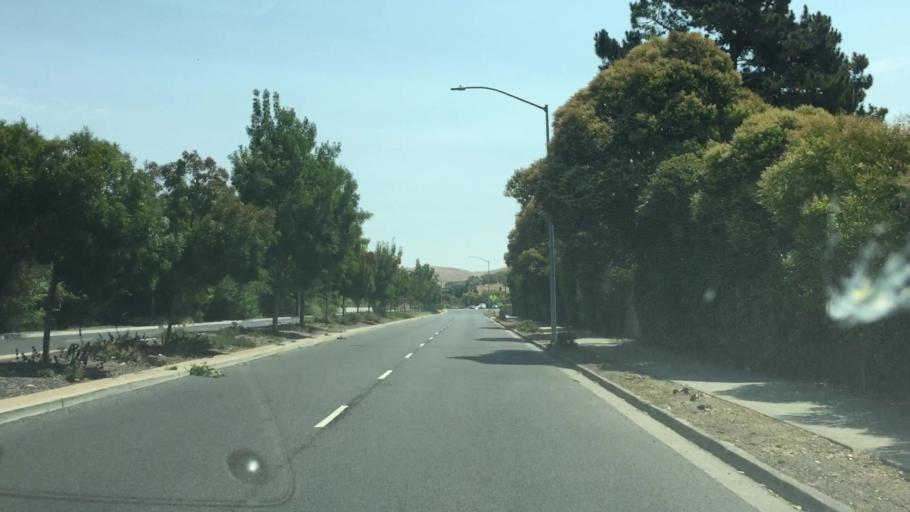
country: US
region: California
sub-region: Napa County
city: American Canyon
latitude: 38.1650
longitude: -122.2430
